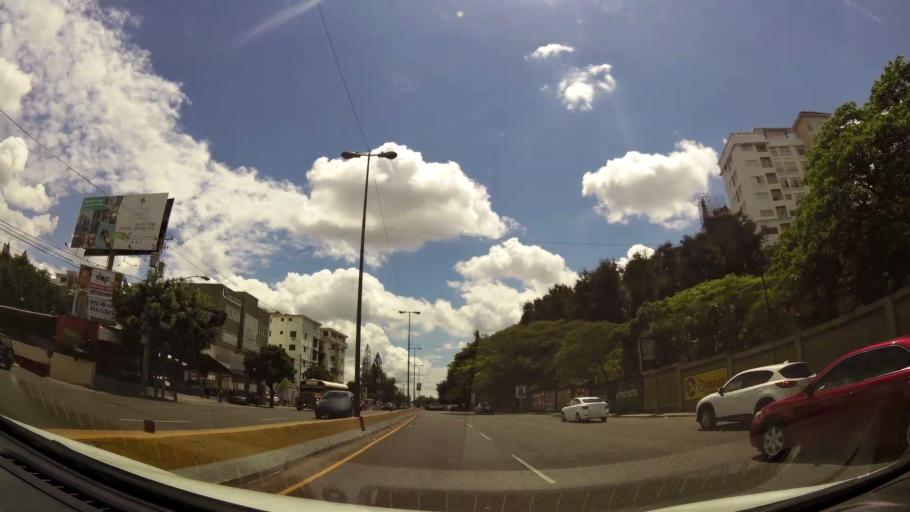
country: DO
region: Santiago
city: Santiago de los Caballeros
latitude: 19.4561
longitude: -70.6854
